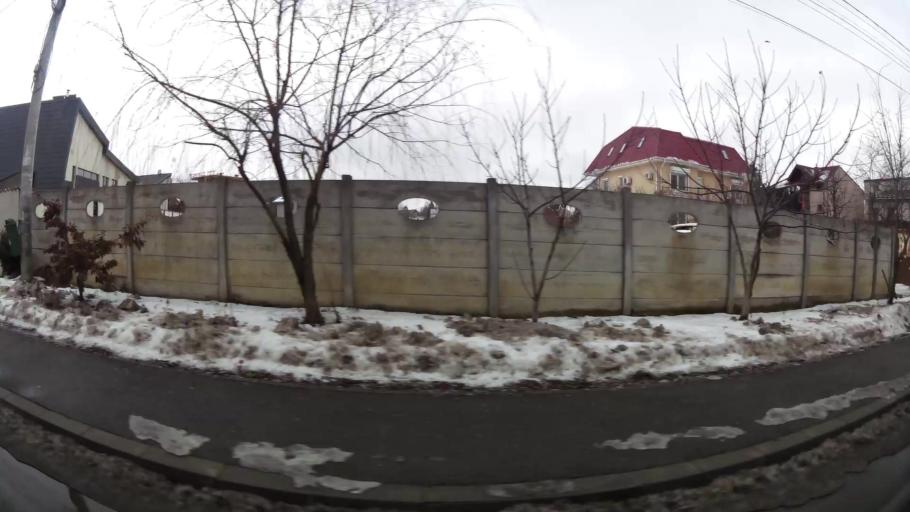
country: RO
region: Ilfov
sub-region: Comuna Otopeni
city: Otopeni
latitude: 44.5067
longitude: 26.0532
